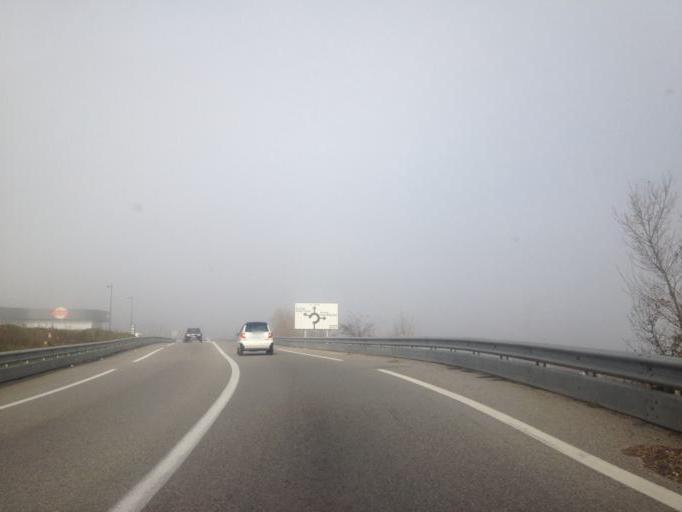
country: FR
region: Rhone-Alpes
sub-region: Departement de l'Ardeche
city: Le Teil
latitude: 44.5531
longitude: 4.6908
